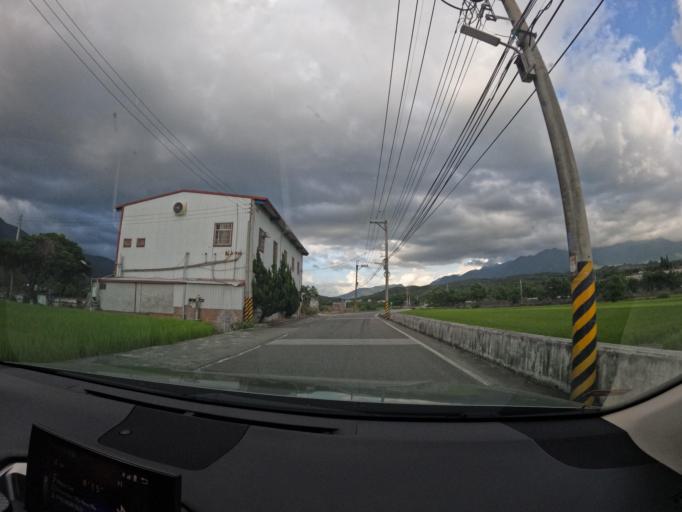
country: TW
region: Taiwan
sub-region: Taitung
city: Taitung
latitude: 23.1554
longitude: 121.2352
